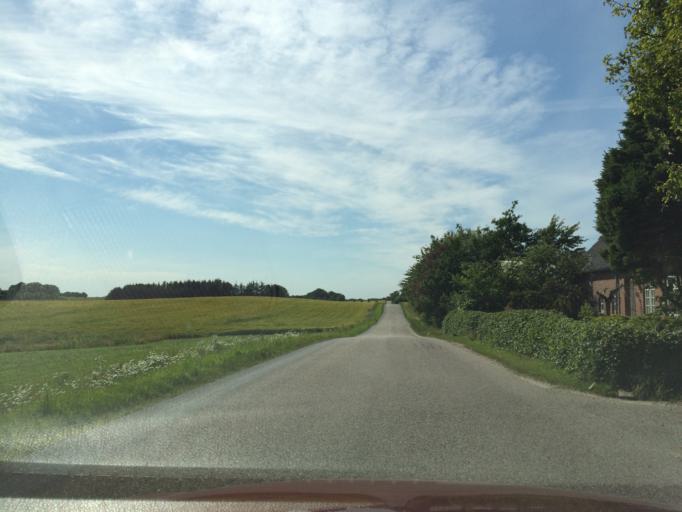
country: DK
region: Central Jutland
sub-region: Silkeborg Kommune
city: Svejbaek
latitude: 56.2253
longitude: 9.6211
